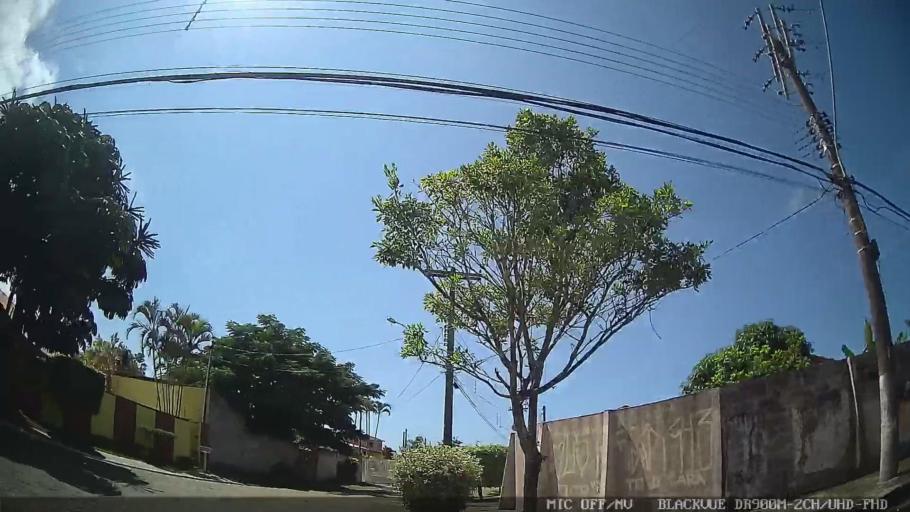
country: BR
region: Sao Paulo
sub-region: Peruibe
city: Peruibe
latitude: -24.3091
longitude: -47.0036
